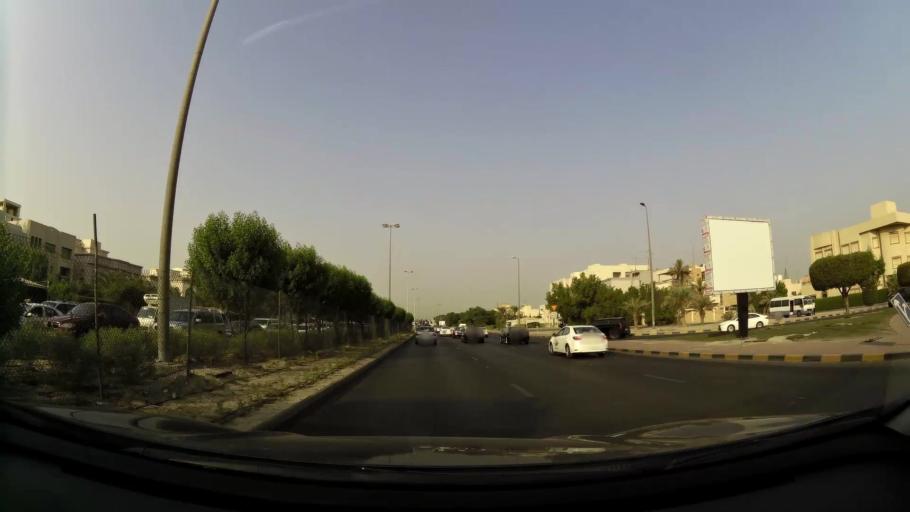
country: KW
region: Muhafazat Hawalli
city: Hawalli
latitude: 29.3213
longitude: 47.9983
